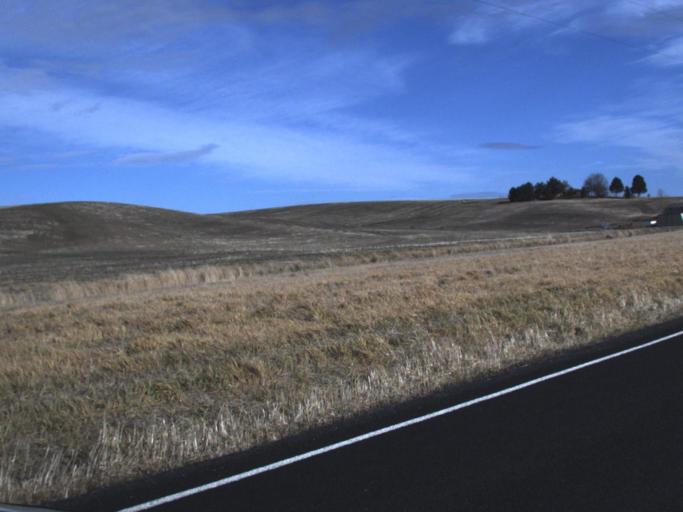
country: US
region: Washington
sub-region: Whitman County
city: Colfax
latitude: 46.9356
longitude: -117.2058
